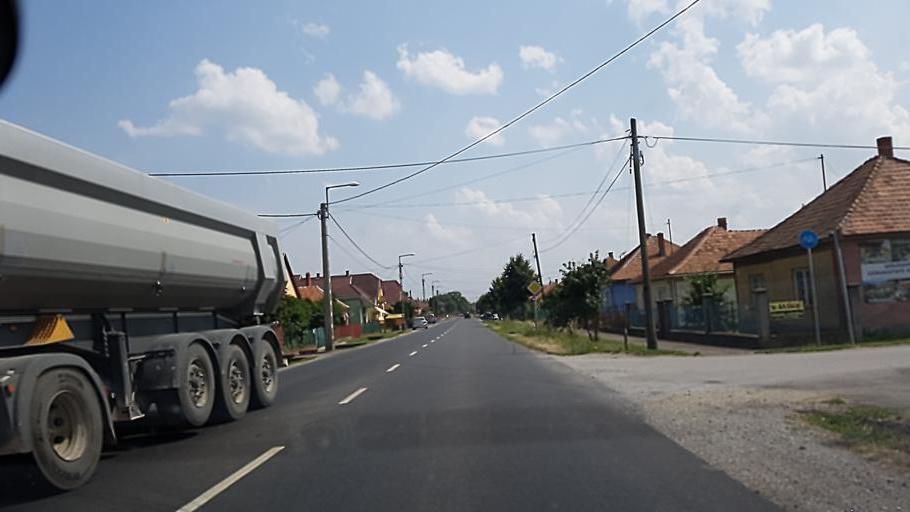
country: HU
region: Heves
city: Besenyotelek
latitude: 47.7094
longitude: 20.4250
